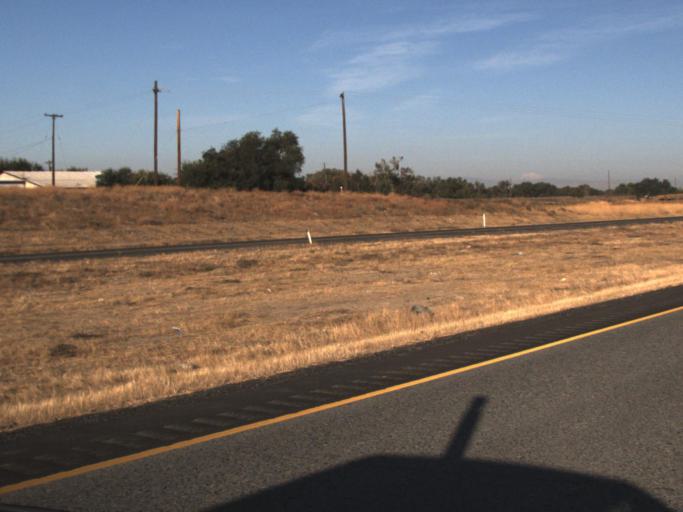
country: US
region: Washington
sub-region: Yakima County
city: Zillah
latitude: 46.3808
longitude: -120.2239
